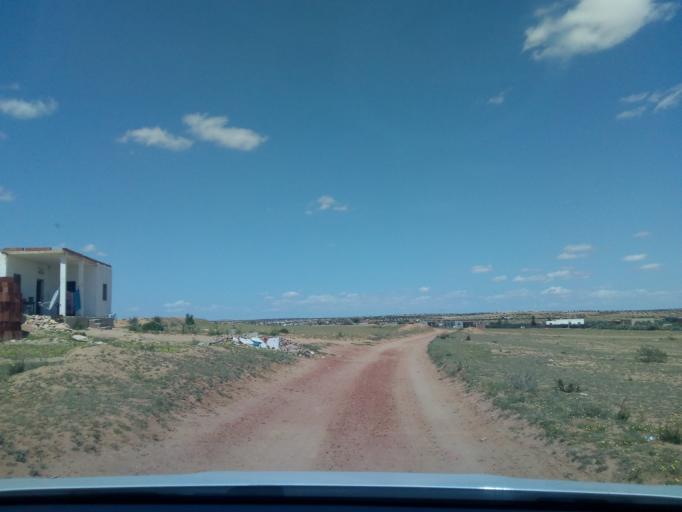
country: TN
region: Safaqis
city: Sfax
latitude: 34.7303
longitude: 10.4976
